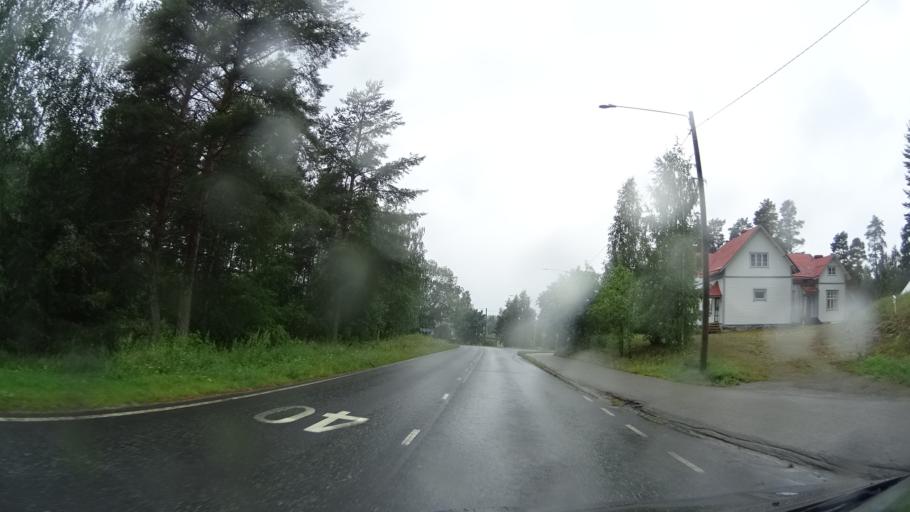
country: FI
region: North Karelia
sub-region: Keski-Karjala
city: Raeaekkylae
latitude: 62.3169
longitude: 29.6127
